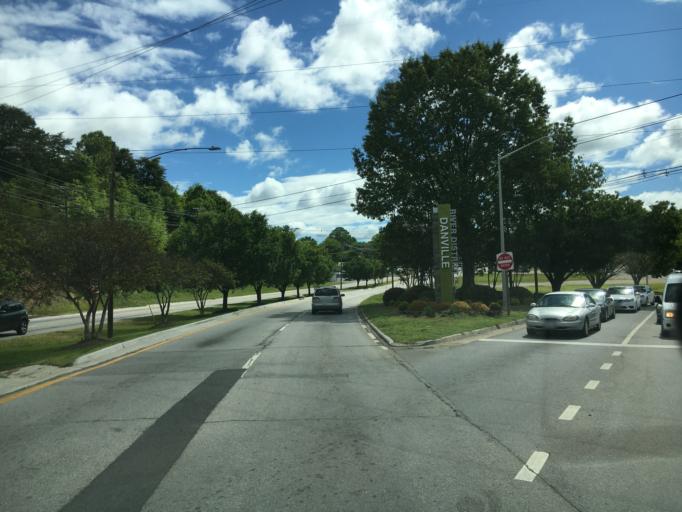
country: US
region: Virginia
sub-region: City of Danville
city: Danville
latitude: 36.5971
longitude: -79.3984
